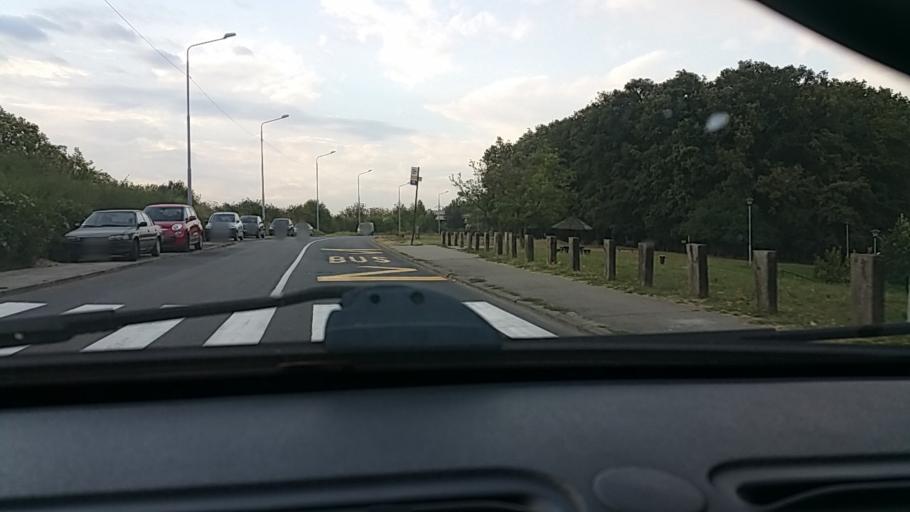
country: RS
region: Central Serbia
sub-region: Belgrade
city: Rakovica
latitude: 44.7461
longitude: 20.4618
